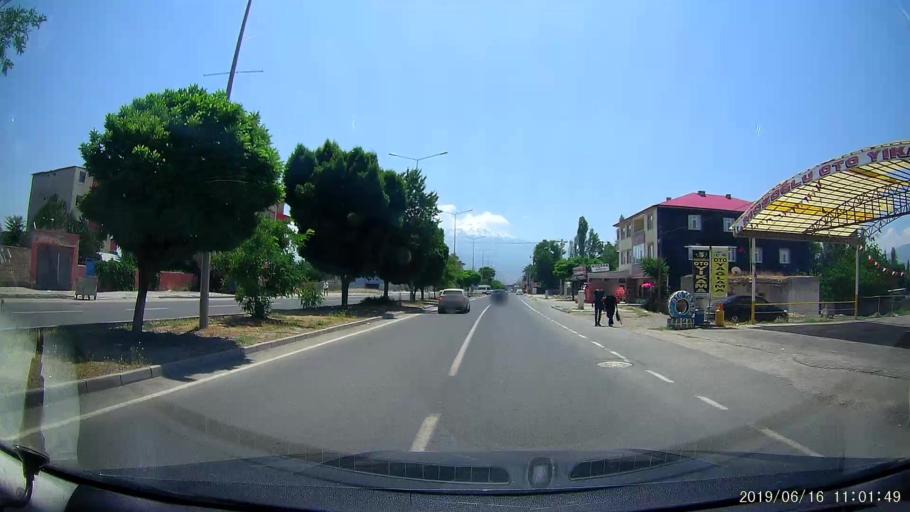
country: TR
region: Igdir
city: Igdir
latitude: 39.9122
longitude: 44.0539
